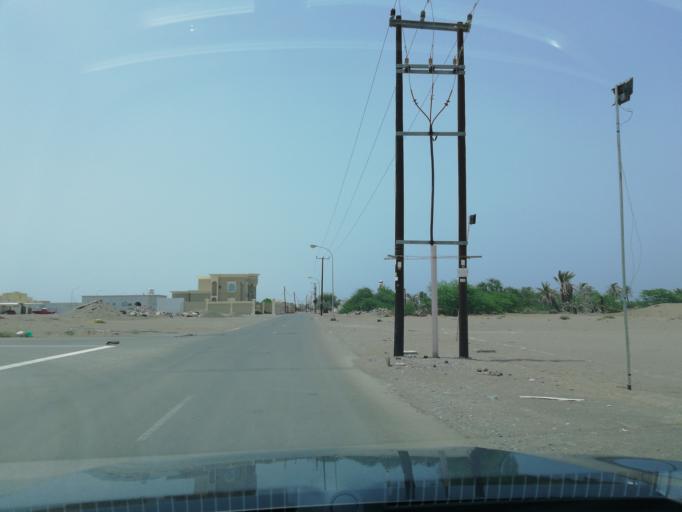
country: OM
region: Al Batinah
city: Al Liwa'
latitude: 24.6139
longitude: 56.5364
